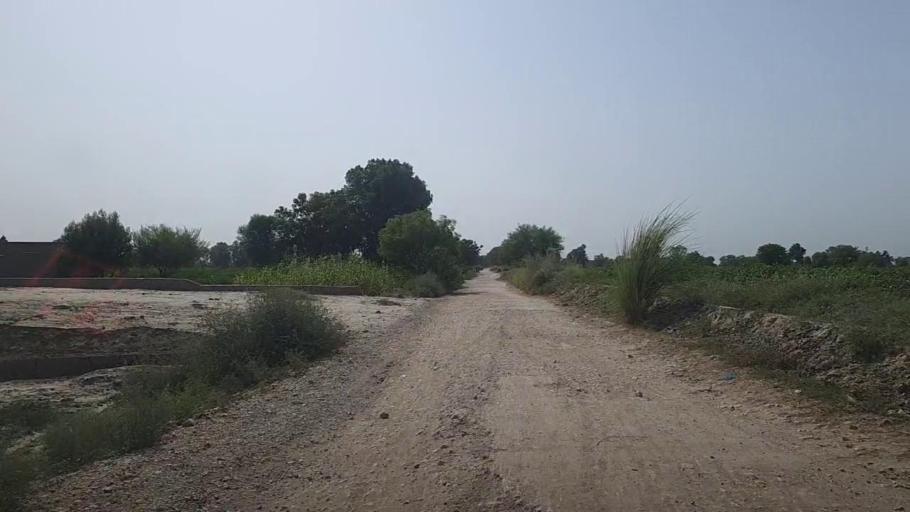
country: PK
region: Sindh
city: Pad Idan
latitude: 26.7658
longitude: 68.3246
